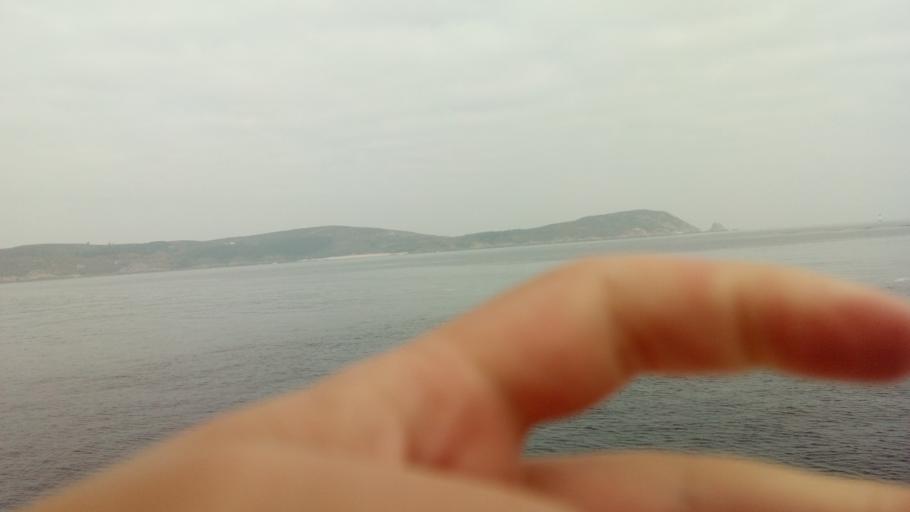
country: ES
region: Galicia
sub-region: Provincia de Pontevedra
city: Sanxenxo
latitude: 42.3792
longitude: -8.9050
